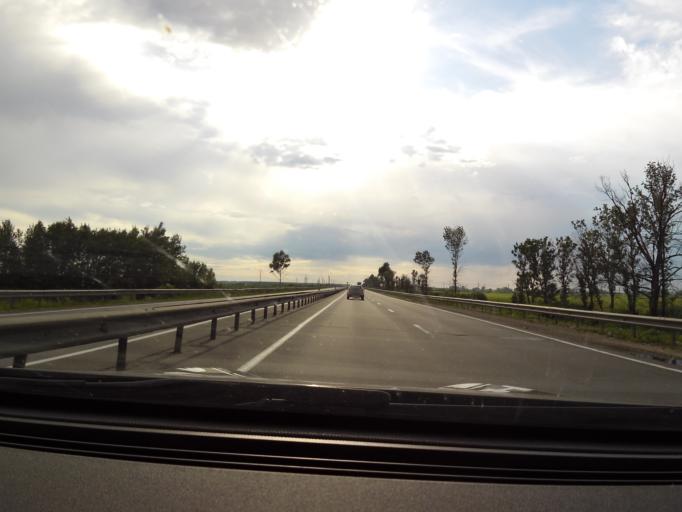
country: RU
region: Vladimir
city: Novovyazniki
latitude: 56.2179
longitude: 42.2143
